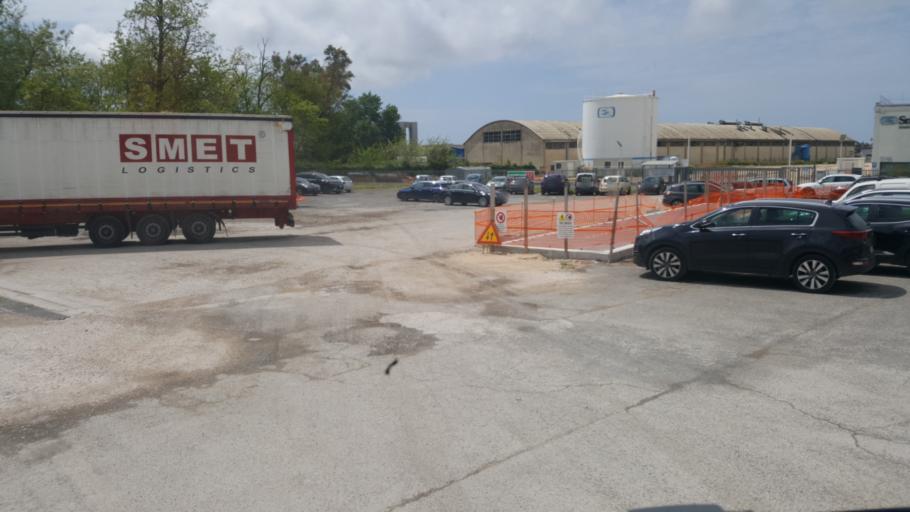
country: IT
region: Latium
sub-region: Citta metropolitana di Roma Capitale
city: Anzio
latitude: 41.5156
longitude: 12.6287
